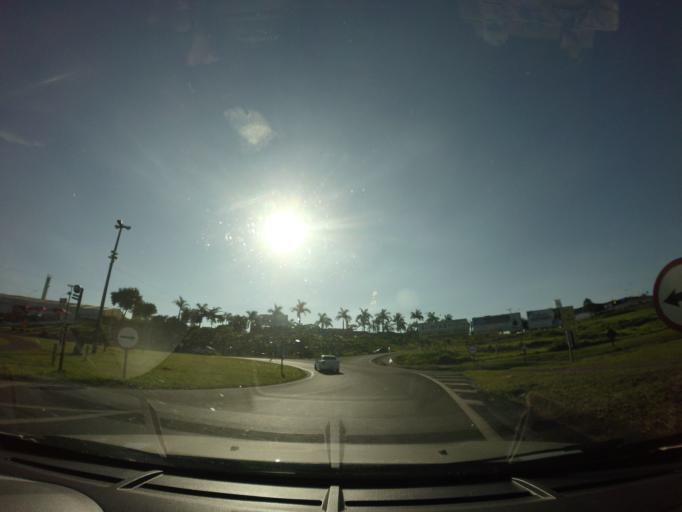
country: BR
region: Sao Paulo
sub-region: Rio Claro
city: Rio Claro
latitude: -22.4199
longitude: -47.5784
